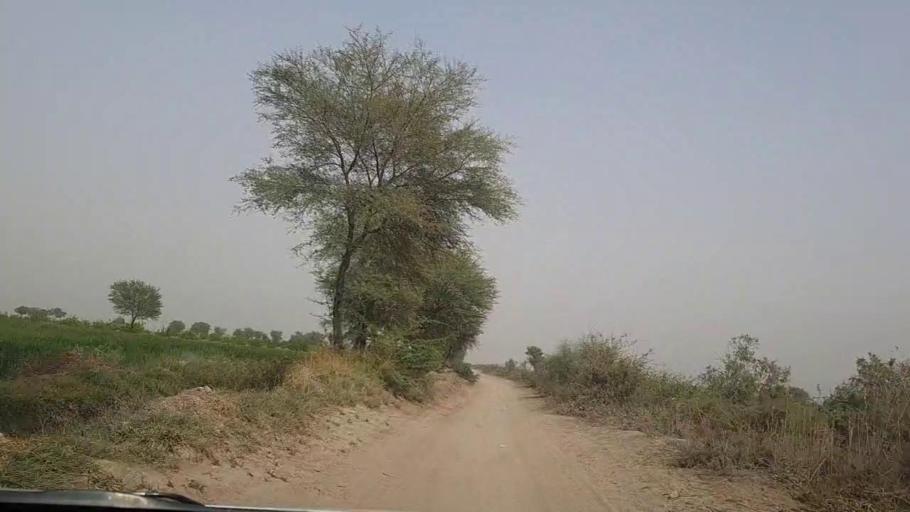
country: PK
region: Sindh
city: Pithoro
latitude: 25.4582
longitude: 69.2497
